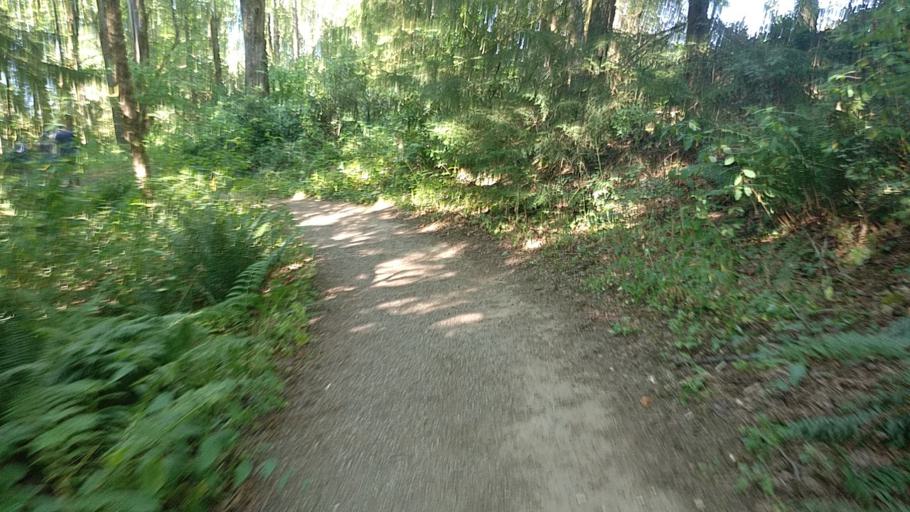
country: CA
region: British Columbia
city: Abbotsford
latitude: 49.1527
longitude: -122.2720
